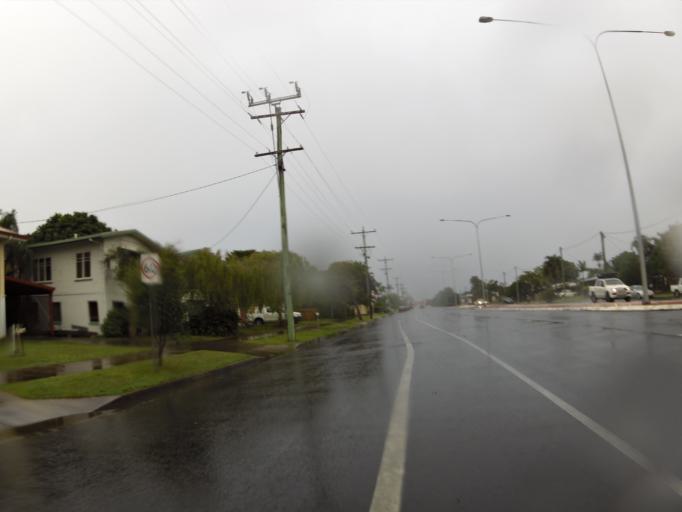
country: AU
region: Queensland
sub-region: Cairns
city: Cairns
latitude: -16.9255
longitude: 145.7543
